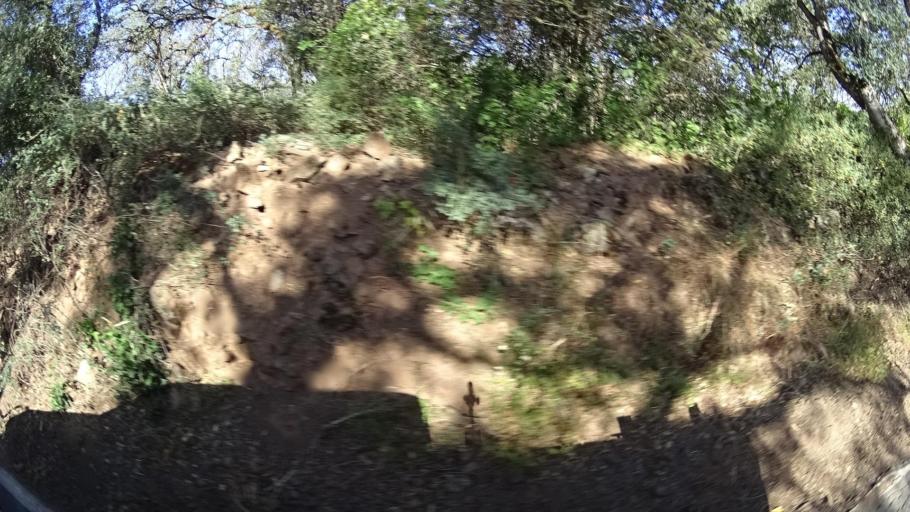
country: US
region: California
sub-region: Lake County
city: Clearlake Oaks
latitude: 39.0117
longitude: -122.6490
